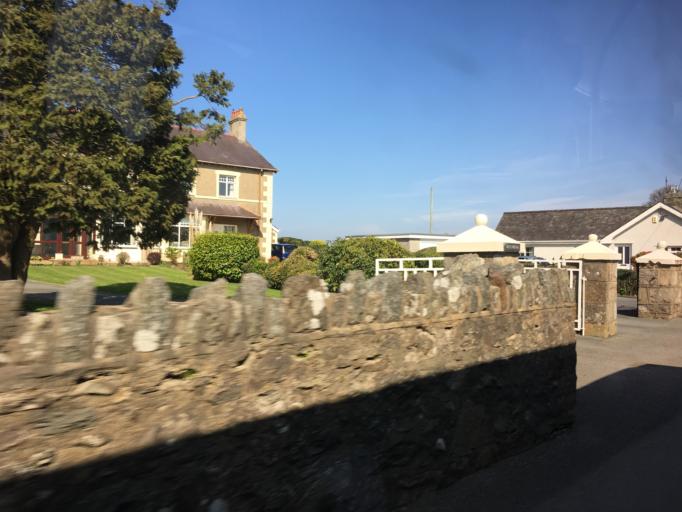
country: GB
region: Wales
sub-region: Gwynedd
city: Llanwnda
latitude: 53.0945
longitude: -4.2770
